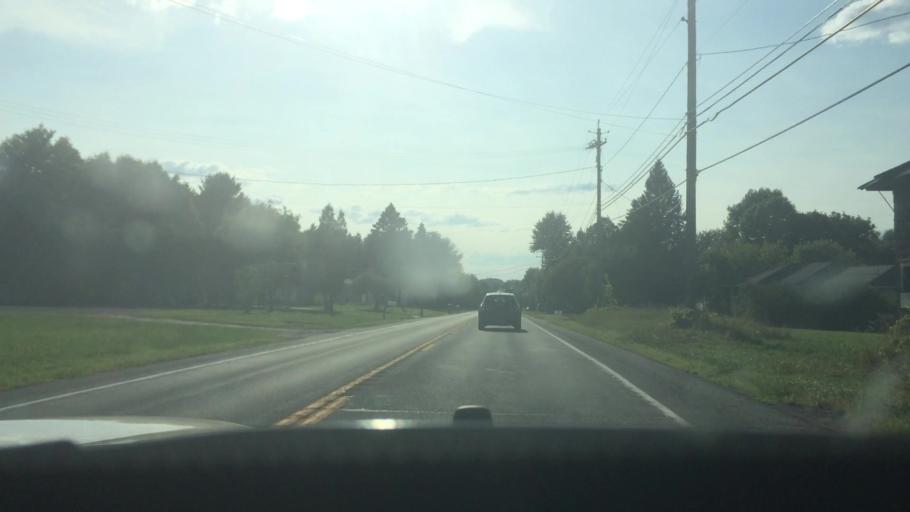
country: US
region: New York
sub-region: St. Lawrence County
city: Potsdam
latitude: 44.6701
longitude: -74.9360
